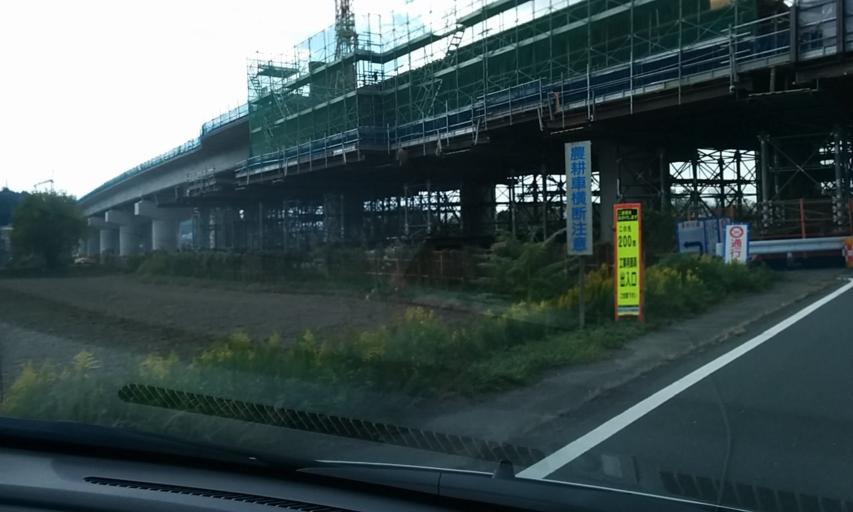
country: JP
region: Kyoto
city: Ayabe
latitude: 35.3069
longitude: 135.1929
